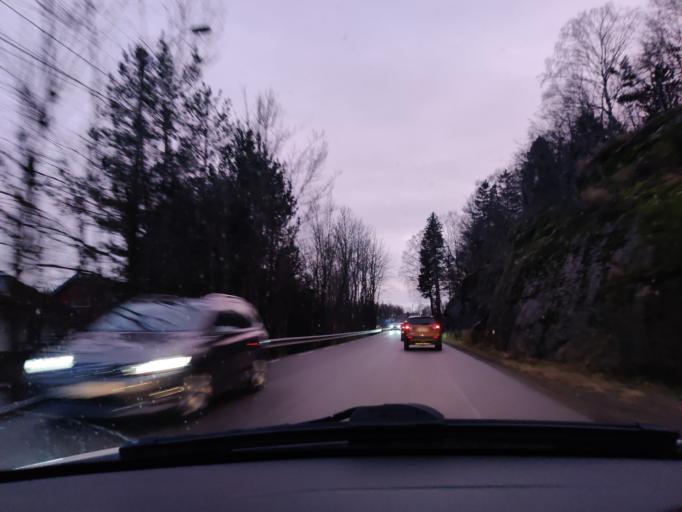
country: NO
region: Vestfold
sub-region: Tonsberg
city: Sem
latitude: 59.2715
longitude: 10.3662
